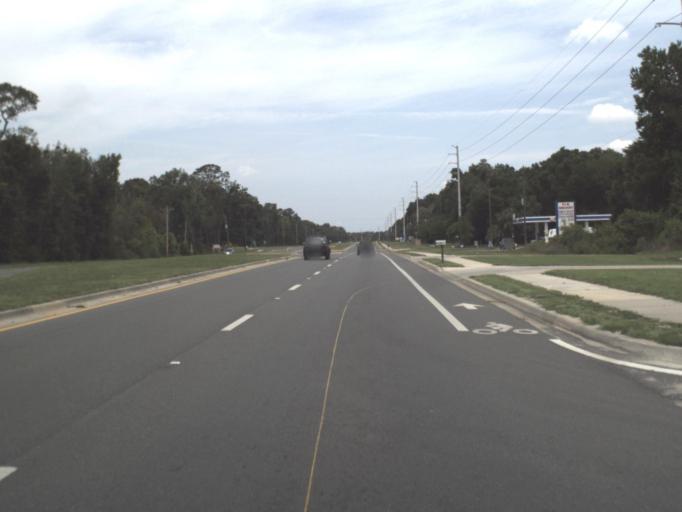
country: US
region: Florida
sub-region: Putnam County
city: Interlachen
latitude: 29.6270
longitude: -81.8625
